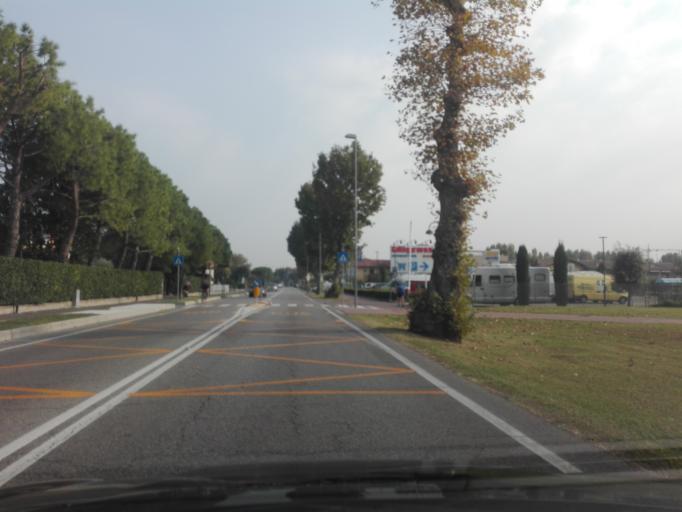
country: IT
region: Lombardy
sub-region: Provincia di Brescia
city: San Martino della Battaglia
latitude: 45.4643
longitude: 10.6136
